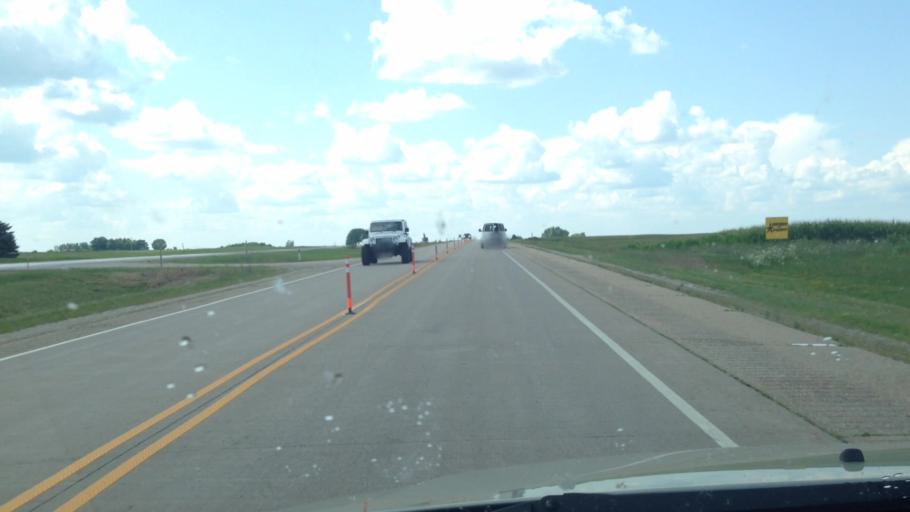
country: US
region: Wisconsin
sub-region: Shawano County
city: Bonduel
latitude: 44.6984
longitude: -88.3551
